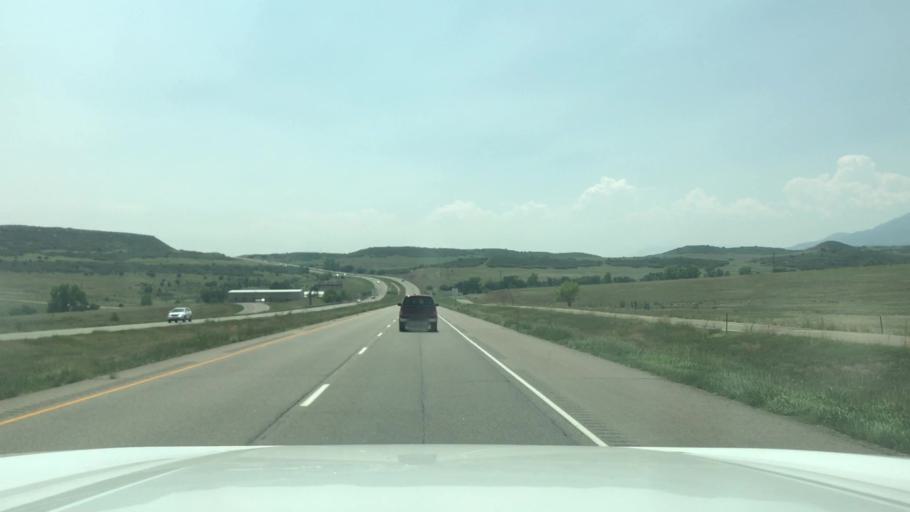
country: US
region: Colorado
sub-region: Pueblo County
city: Colorado City
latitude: 37.9194
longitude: -104.8250
